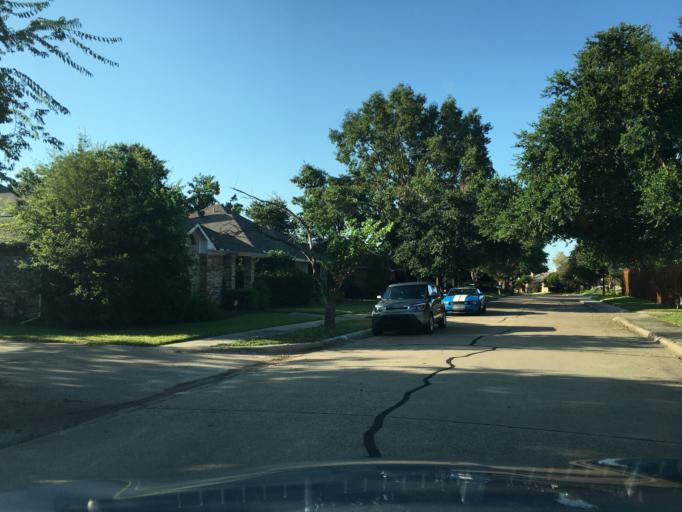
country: US
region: Texas
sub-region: Dallas County
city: Addison
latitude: 32.9690
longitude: -96.8559
